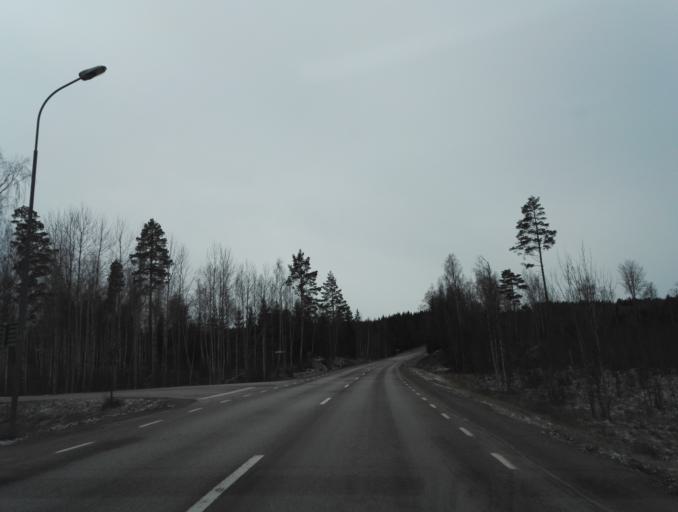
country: SE
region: Kalmar
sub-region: Hultsfreds Kommun
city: Virserum
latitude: 57.3063
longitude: 15.5842
